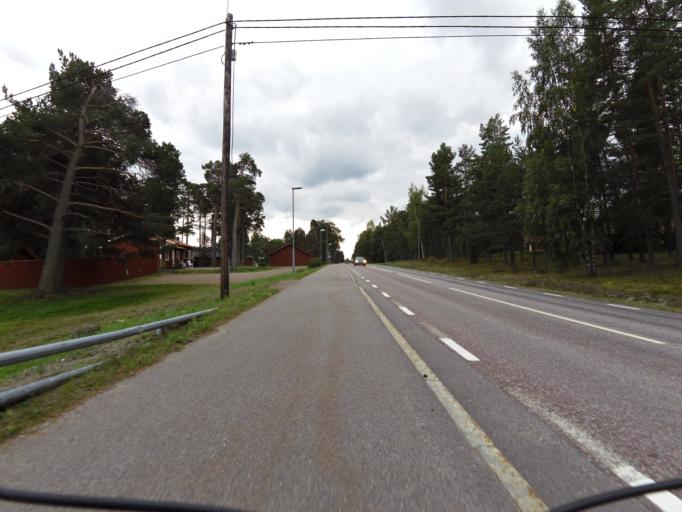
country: SE
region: Gaevleborg
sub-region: Sandvikens Kommun
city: Sandviken
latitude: 60.6733
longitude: 16.8108
